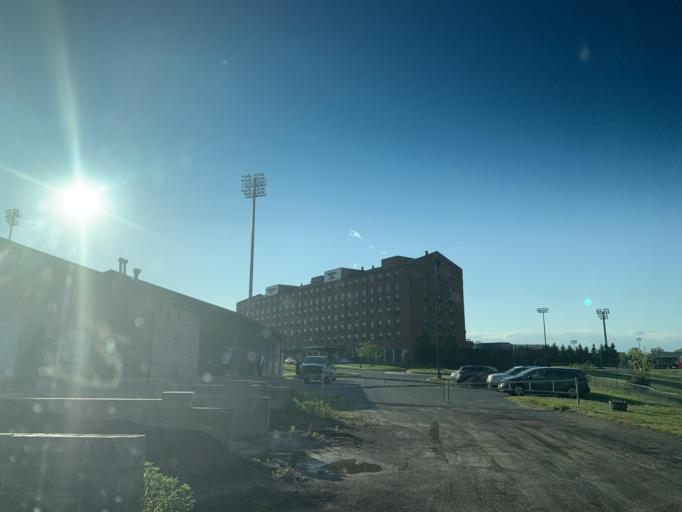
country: US
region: Maryland
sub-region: Harford County
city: Aberdeen
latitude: 39.5313
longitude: -76.1843
